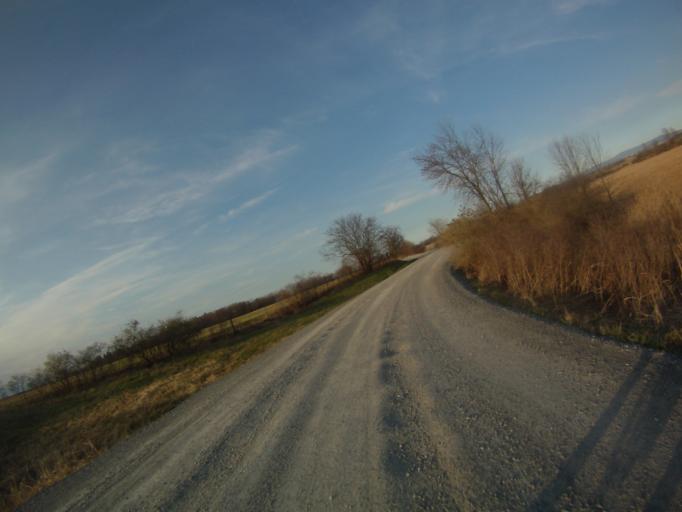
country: US
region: New York
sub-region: Essex County
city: Port Henry
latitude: 44.0806
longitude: -73.3512
